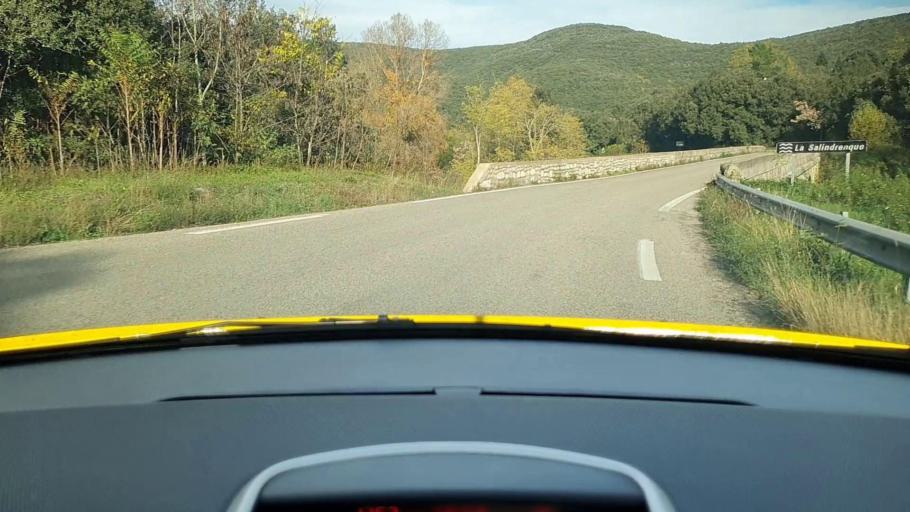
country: FR
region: Languedoc-Roussillon
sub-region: Departement du Gard
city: Anduze
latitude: 44.0705
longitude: 3.9345
